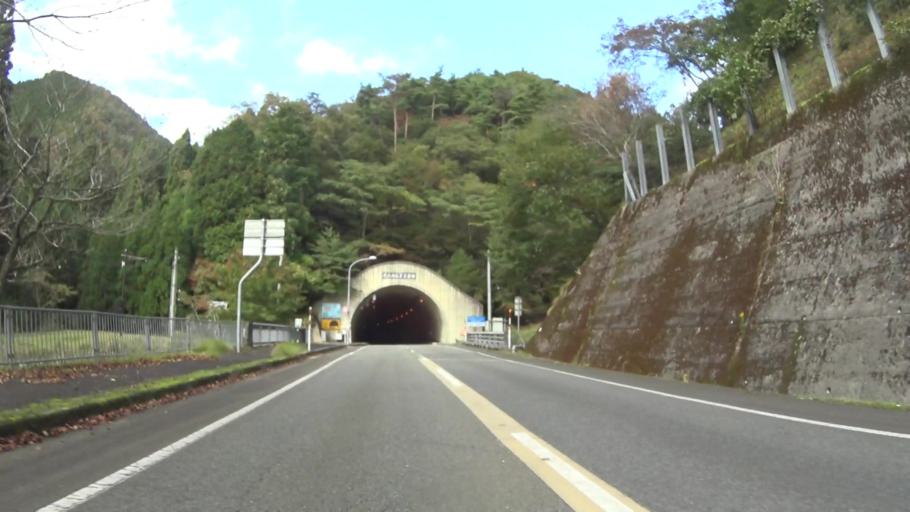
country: JP
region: Hyogo
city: Toyooka
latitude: 35.5235
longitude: 134.9874
